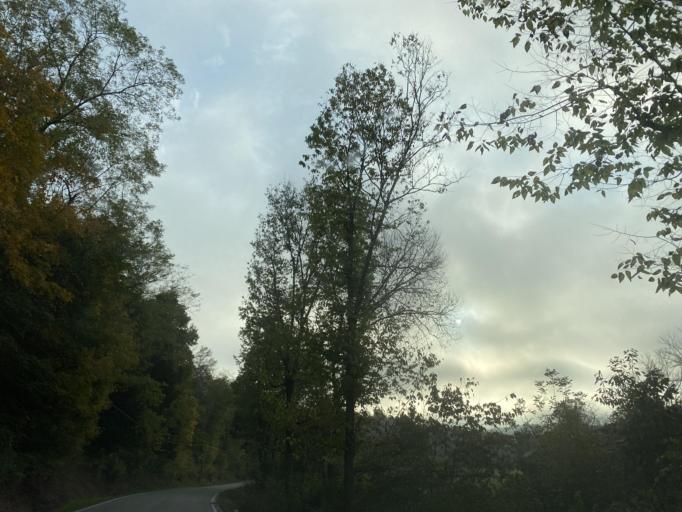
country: US
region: Kentucky
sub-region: Pendleton County
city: Falmouth
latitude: 38.7259
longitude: -84.3056
